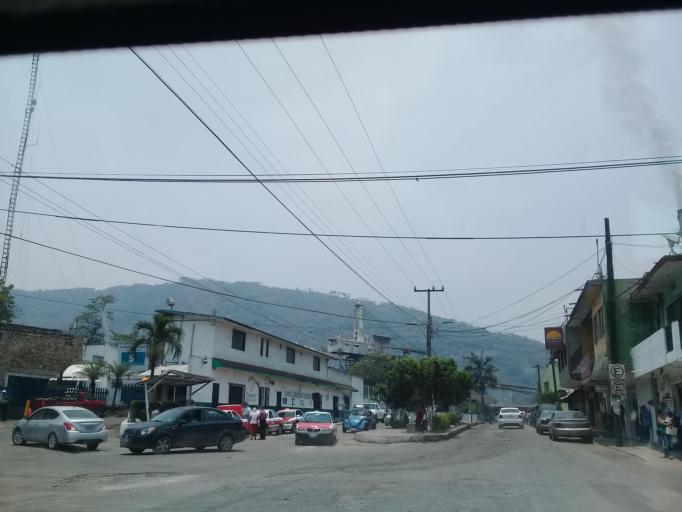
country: MX
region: Veracruz
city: Cosolapa
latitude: 18.6038
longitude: -96.6869
